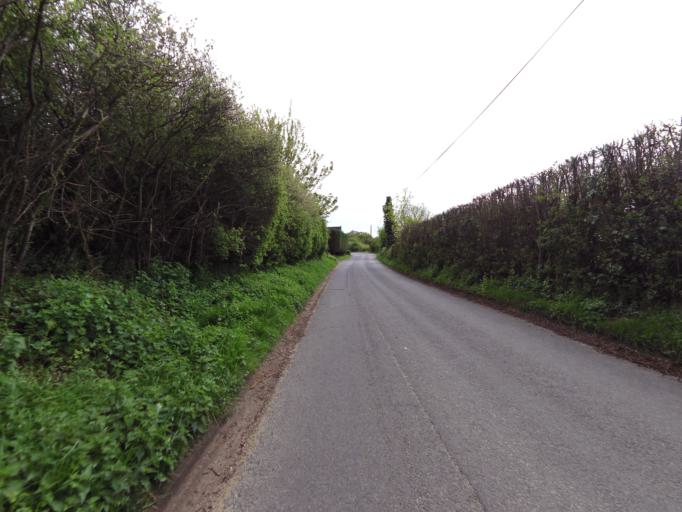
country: GB
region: England
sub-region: Suffolk
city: Ipswich
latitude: 51.9729
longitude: 1.1687
